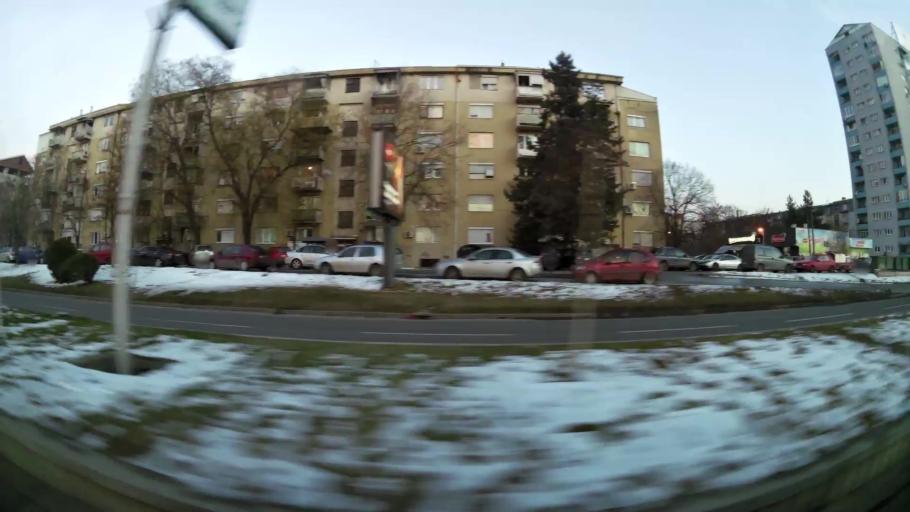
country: MK
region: Karpos
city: Skopje
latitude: 42.0031
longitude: 21.4049
